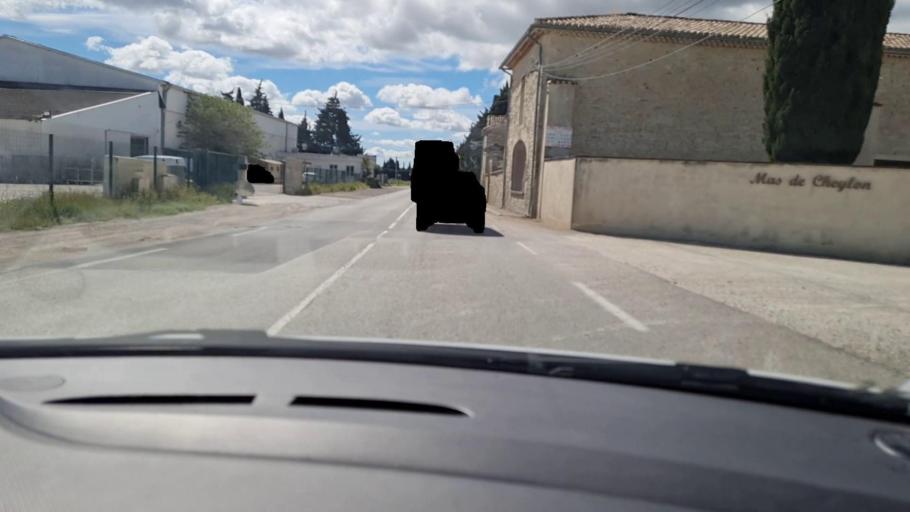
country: FR
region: Languedoc-Roussillon
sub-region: Departement du Gard
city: Milhaud
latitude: 43.8009
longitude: 4.3407
